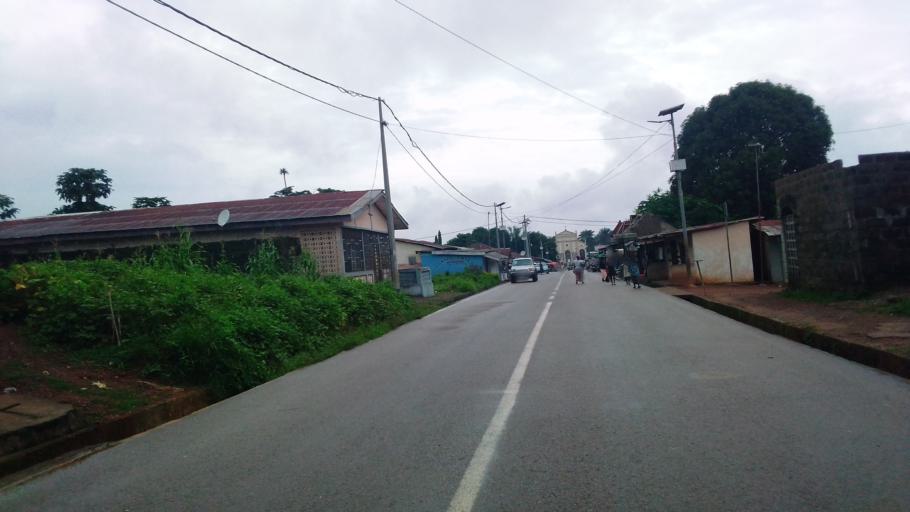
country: SL
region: Northern Province
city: Lunsar
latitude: 8.6842
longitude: -12.5321
